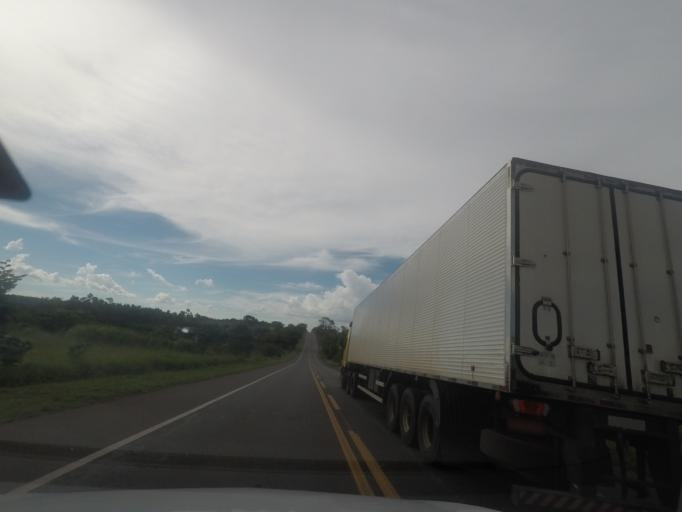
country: BR
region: Minas Gerais
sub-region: Prata
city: Prata
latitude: -19.2897
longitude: -48.9105
